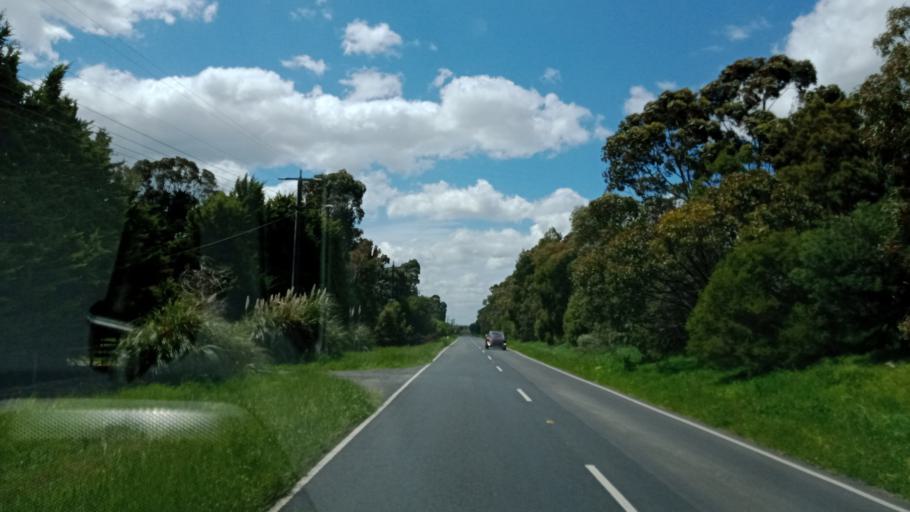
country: AU
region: Victoria
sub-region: Kingston
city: Patterson Lakes
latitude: -38.0470
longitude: 145.1670
